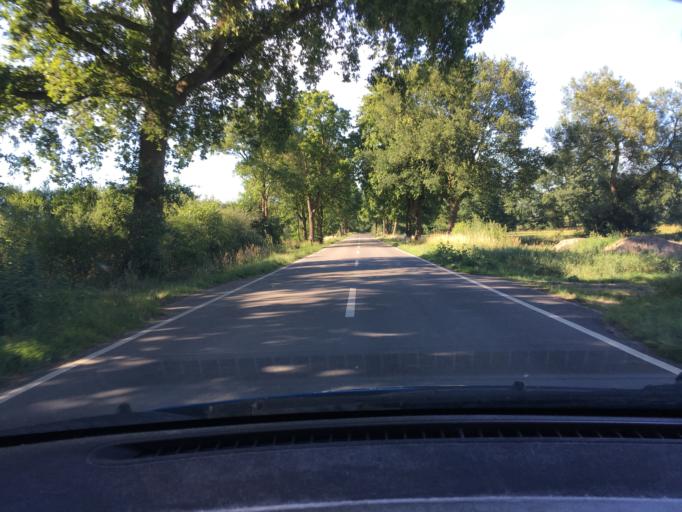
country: DE
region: Lower Saxony
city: Bleckede
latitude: 53.3231
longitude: 10.6749
